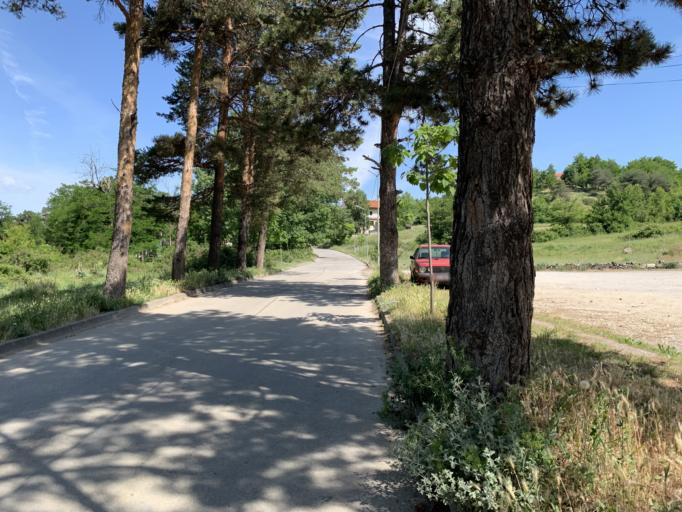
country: AL
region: Korce
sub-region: Rrethi i Korces
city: Korce
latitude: 40.6140
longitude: 20.7893
